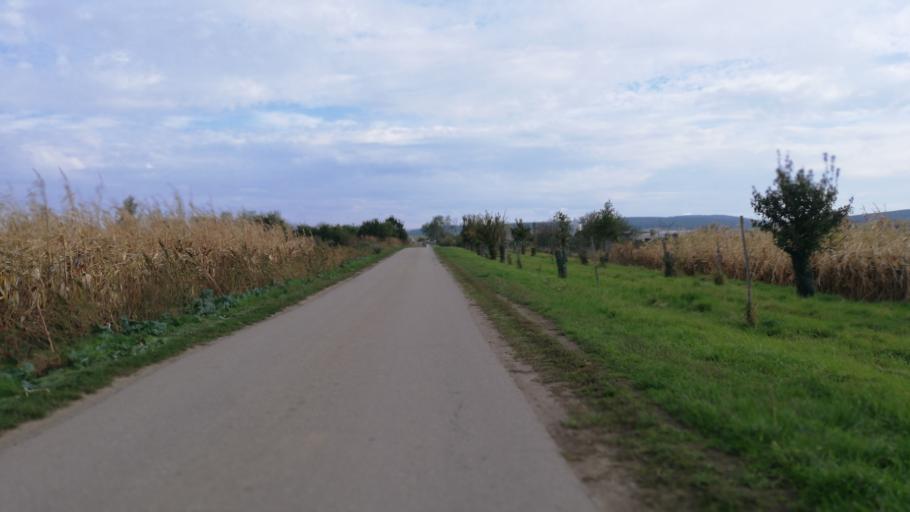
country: CZ
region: South Moravian
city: Sudomerice
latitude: 48.8509
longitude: 17.2461
